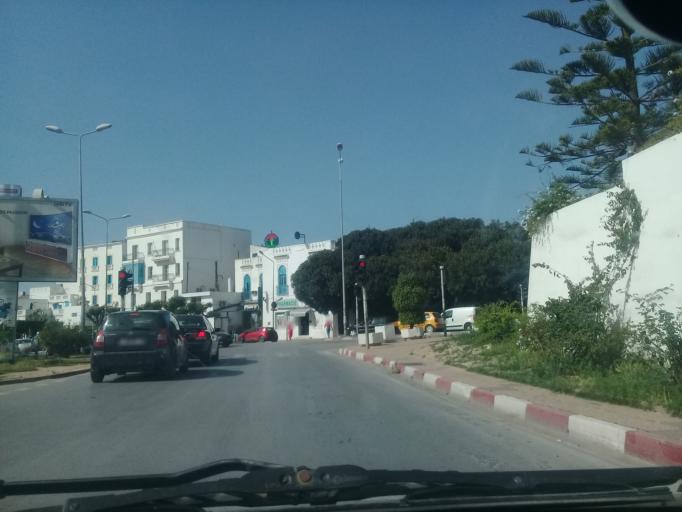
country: TN
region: Tunis
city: Al Marsa
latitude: 36.8789
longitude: 10.3275
